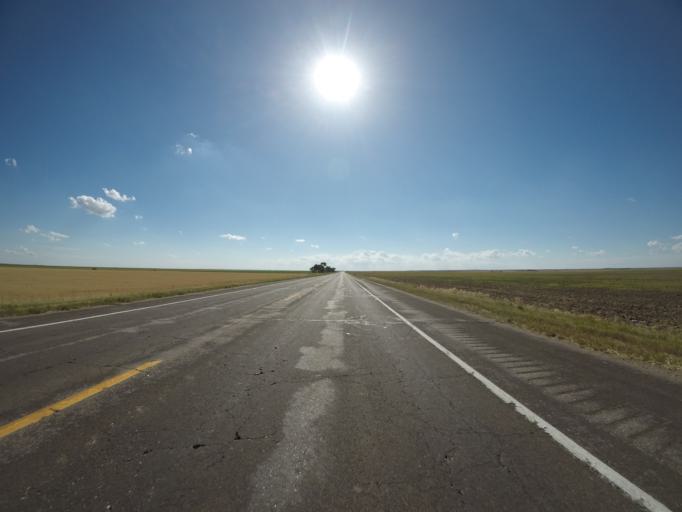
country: US
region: Colorado
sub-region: Logan County
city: Sterling
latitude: 40.6238
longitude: -103.3410
